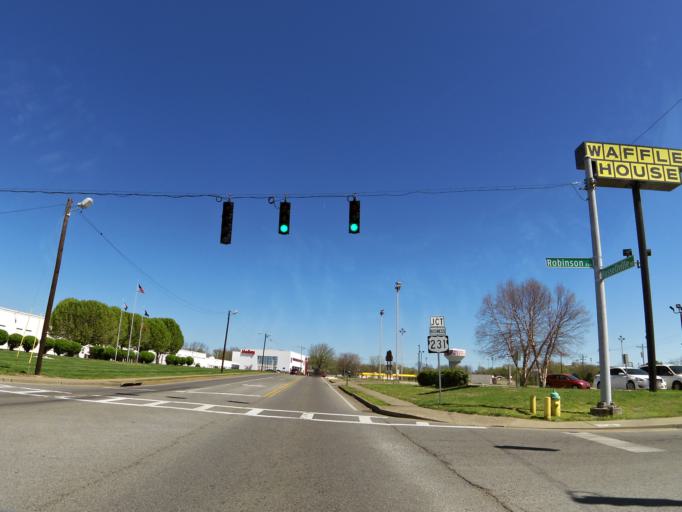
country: US
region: Kentucky
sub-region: Warren County
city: Bowling Green
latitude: 36.9798
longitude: -86.4677
